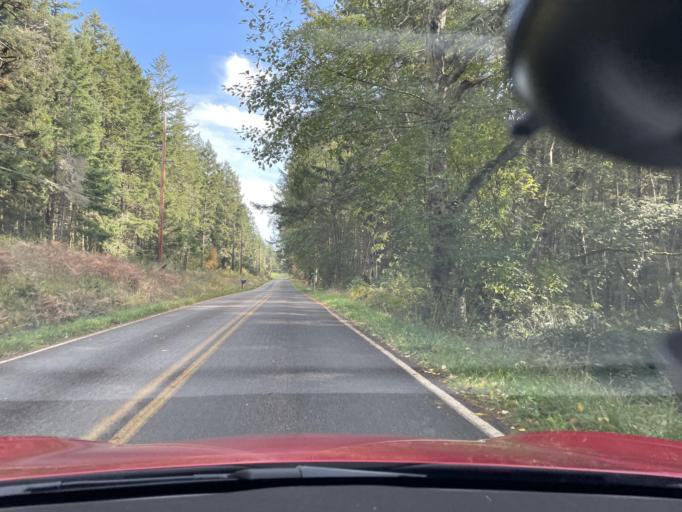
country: US
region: Washington
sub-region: San Juan County
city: Friday Harbor
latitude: 48.5186
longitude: -122.9943
